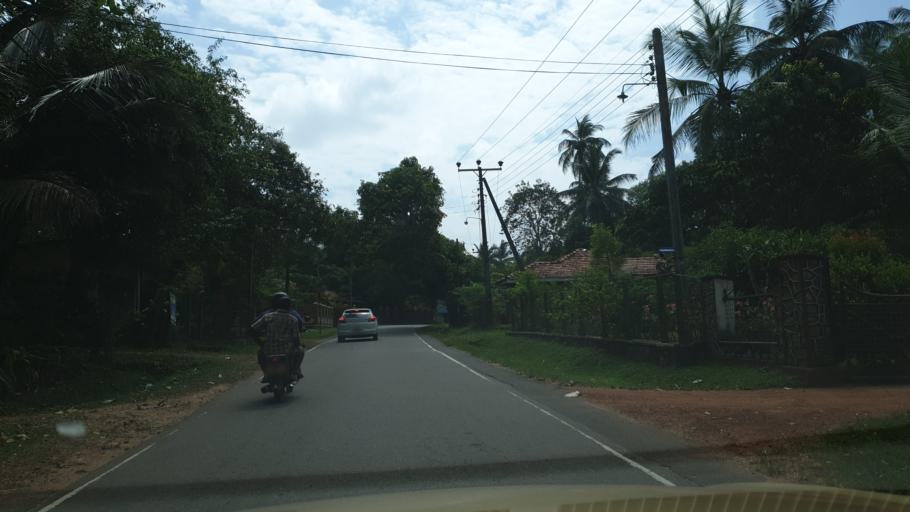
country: LK
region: North Western
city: Kuliyapitiya
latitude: 7.3453
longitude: 79.9863
